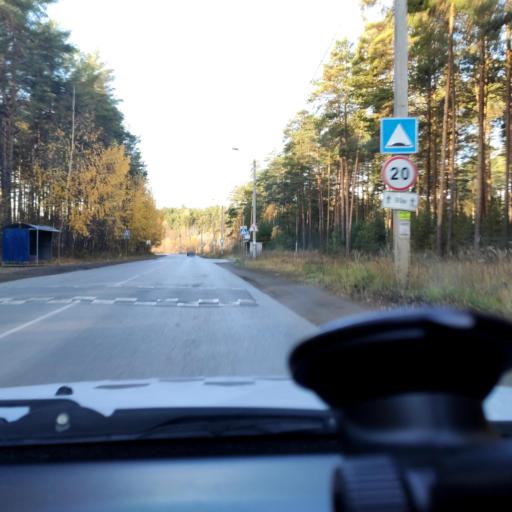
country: RU
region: Perm
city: Perm
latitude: 58.0461
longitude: 56.2765
